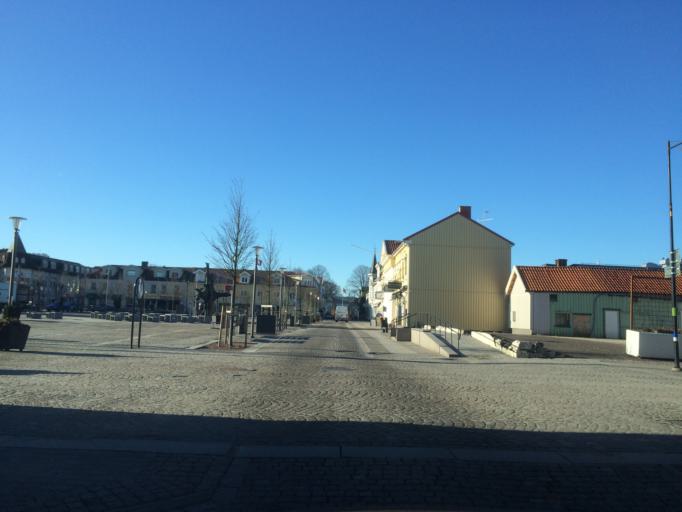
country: SE
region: Halland
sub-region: Kungsbacka Kommun
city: Kungsbacka
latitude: 57.4878
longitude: 12.0766
